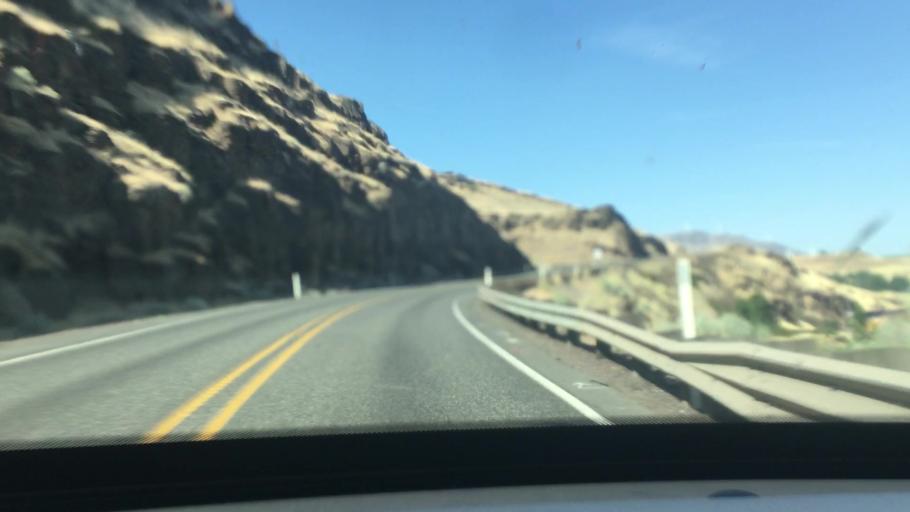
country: US
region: Washington
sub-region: Klickitat County
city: Goldendale
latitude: 45.6848
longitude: -120.8293
